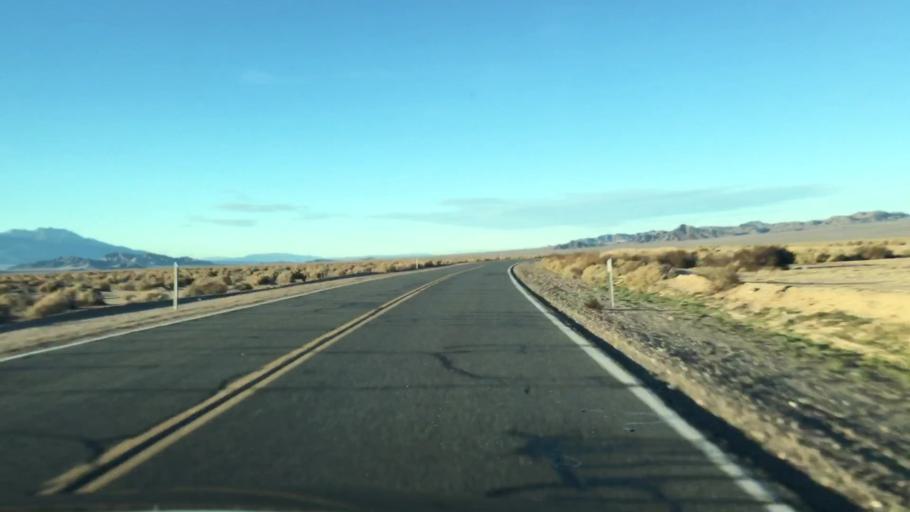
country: US
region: California
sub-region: San Bernardino County
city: Fort Irwin
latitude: 35.2936
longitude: -116.0824
